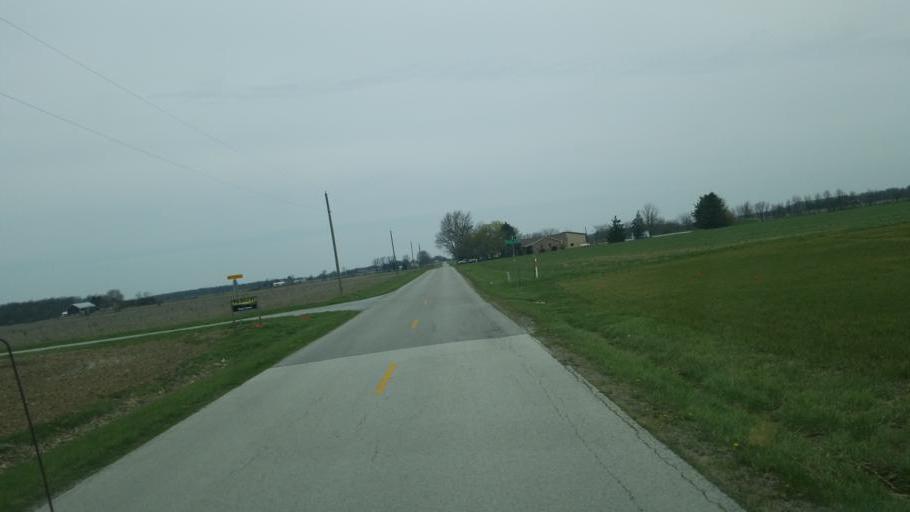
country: US
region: Ohio
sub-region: Seneca County
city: Fostoria
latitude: 41.0572
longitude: -83.4392
